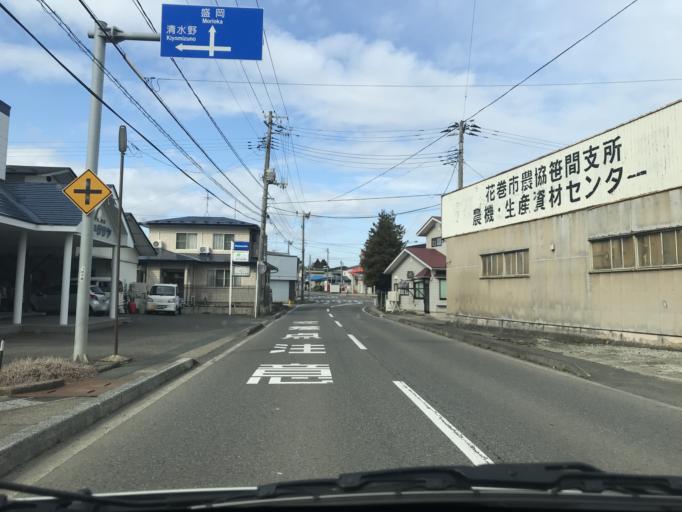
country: JP
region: Iwate
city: Hanamaki
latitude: 39.3602
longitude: 141.0507
